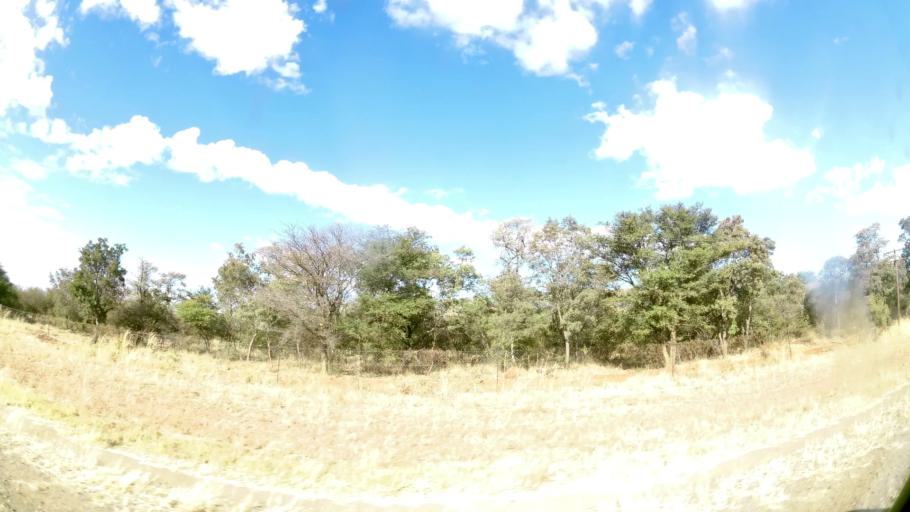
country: ZA
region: Limpopo
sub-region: Waterberg District Municipality
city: Bela-Bela
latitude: -24.8969
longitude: 28.3204
